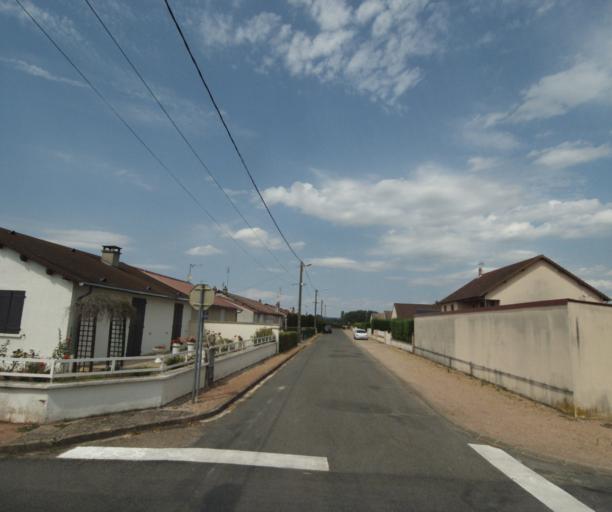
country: FR
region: Bourgogne
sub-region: Departement de Saone-et-Loire
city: Gueugnon
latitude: 46.6076
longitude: 4.0542
